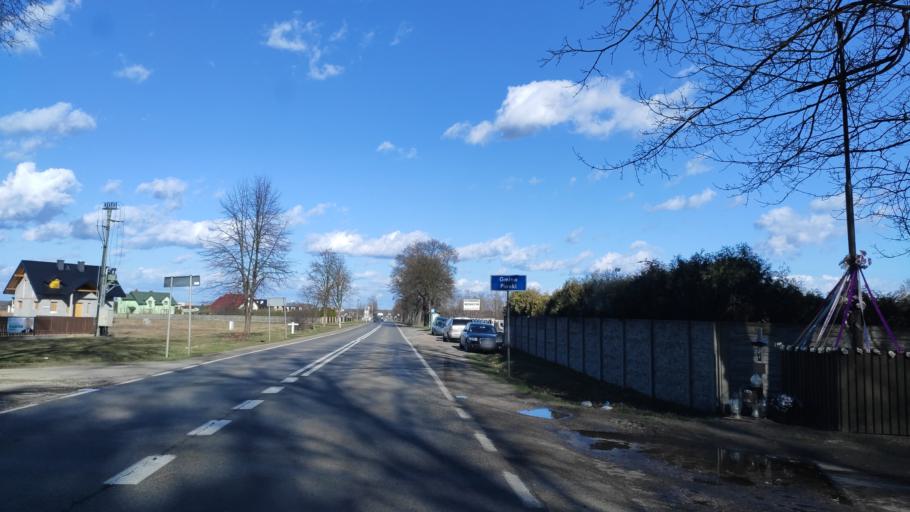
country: PL
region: Masovian Voivodeship
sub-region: Powiat radomski
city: Jedlnia-Letnisko
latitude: 51.4475
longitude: 21.3270
